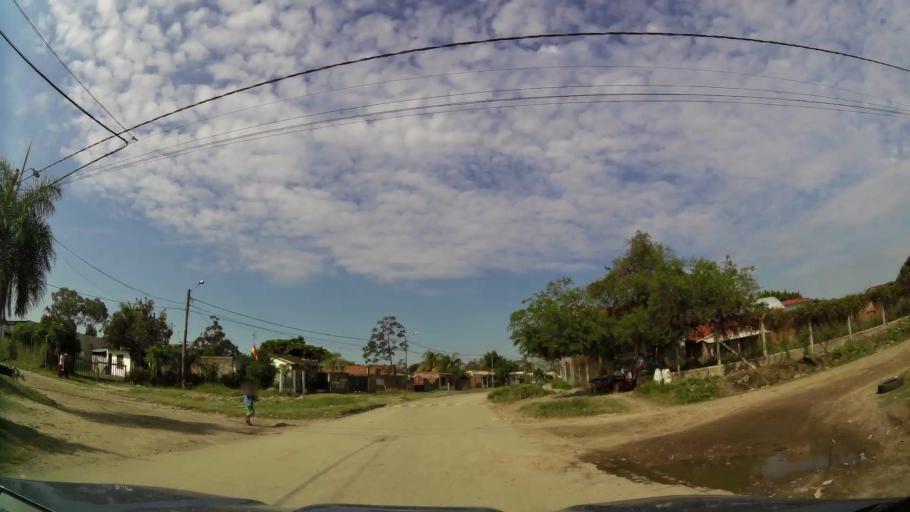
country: BO
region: Santa Cruz
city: Santa Cruz de la Sierra
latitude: -17.7326
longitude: -63.1337
